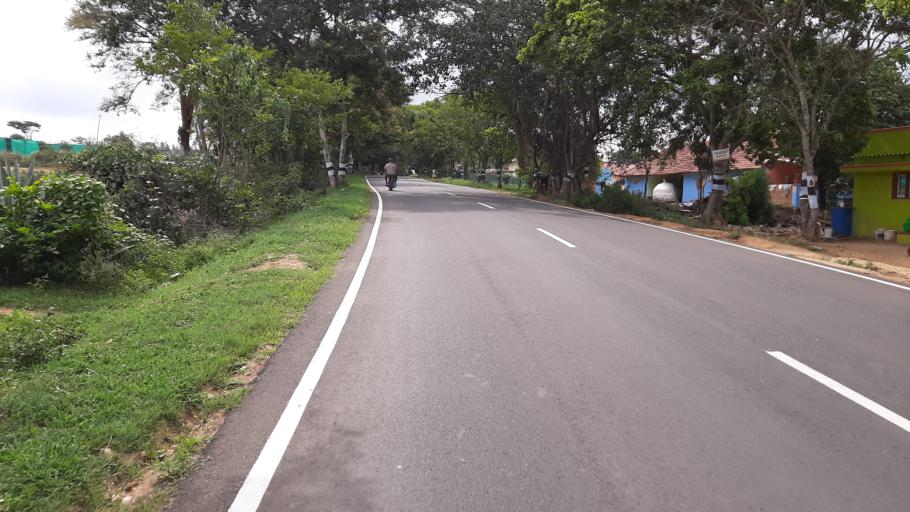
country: IN
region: Tamil Nadu
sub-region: Krishnagiri
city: Denkanikota
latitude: 12.5367
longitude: 77.7721
